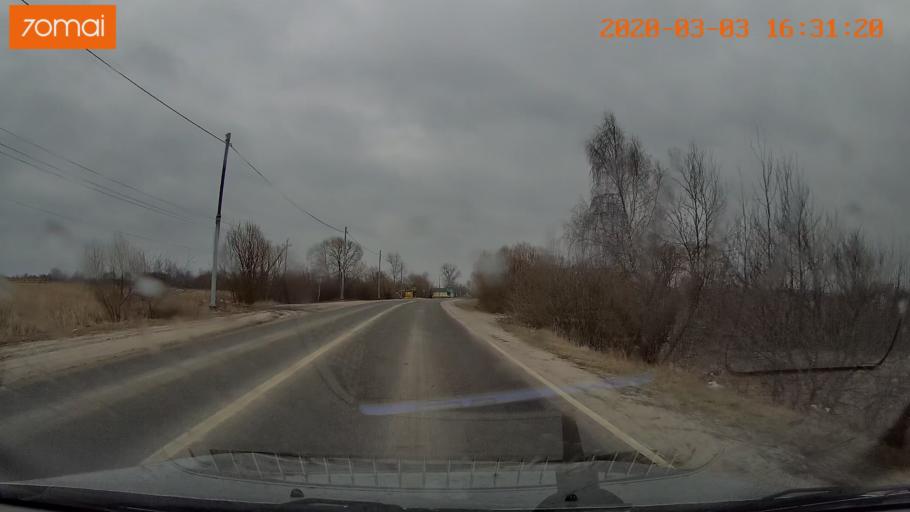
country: RU
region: Moskovskaya
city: Konobeyevo
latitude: 55.4260
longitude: 38.7239
